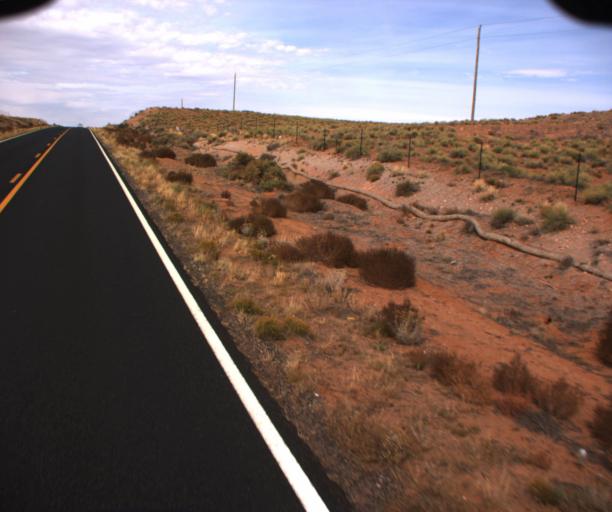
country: US
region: Arizona
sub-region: Apache County
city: Many Farms
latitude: 36.5972
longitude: -109.5669
